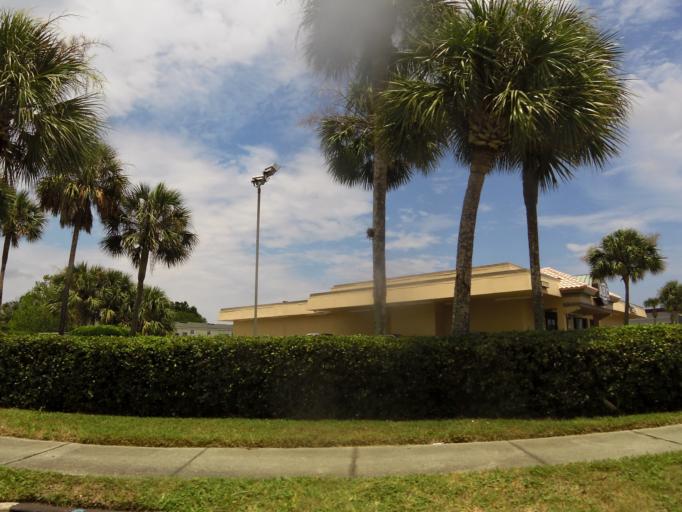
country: US
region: Florida
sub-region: Duval County
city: Atlantic Beach
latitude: 30.3258
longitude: -81.4098
